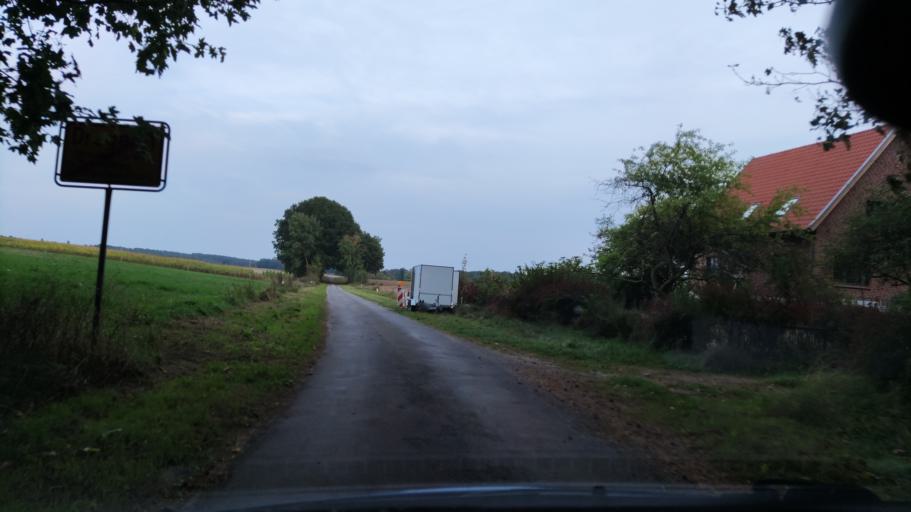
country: DE
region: Lower Saxony
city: Karwitz
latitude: 53.0916
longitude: 10.9823
